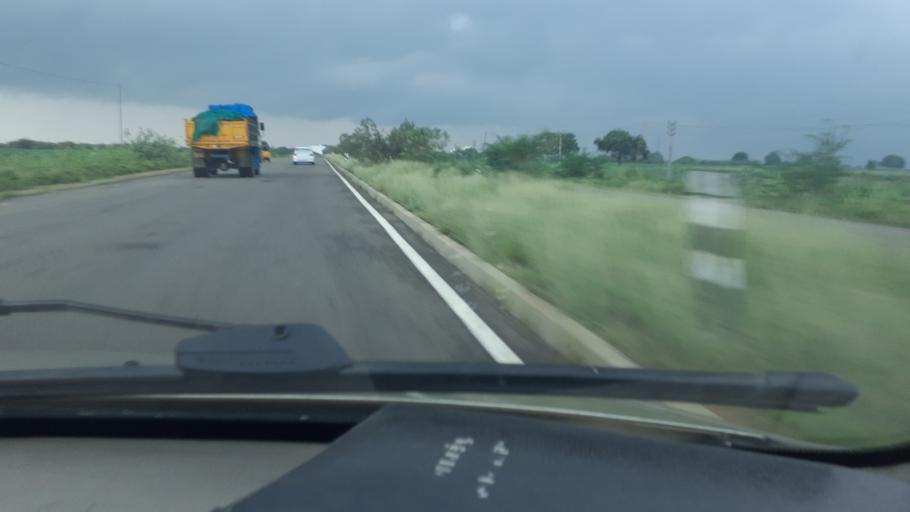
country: IN
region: Tamil Nadu
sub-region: Thoothukkudi
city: Kovilpatti
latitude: 9.1187
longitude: 77.8157
